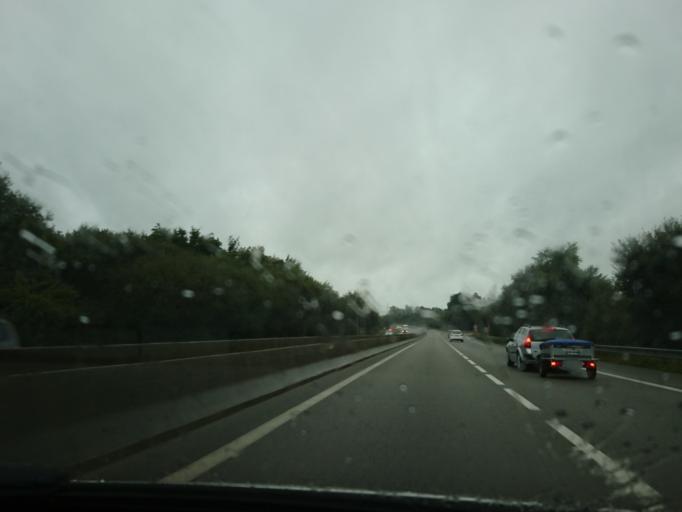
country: FR
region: Brittany
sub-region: Departement du Morbihan
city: Vannes
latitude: 47.6537
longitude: -2.7043
